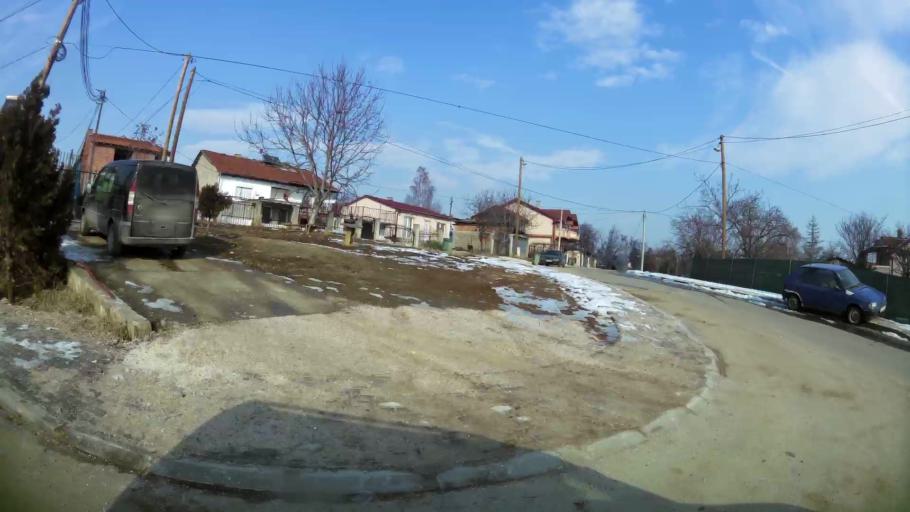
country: MK
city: Creshevo
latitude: 42.0061
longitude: 21.4952
